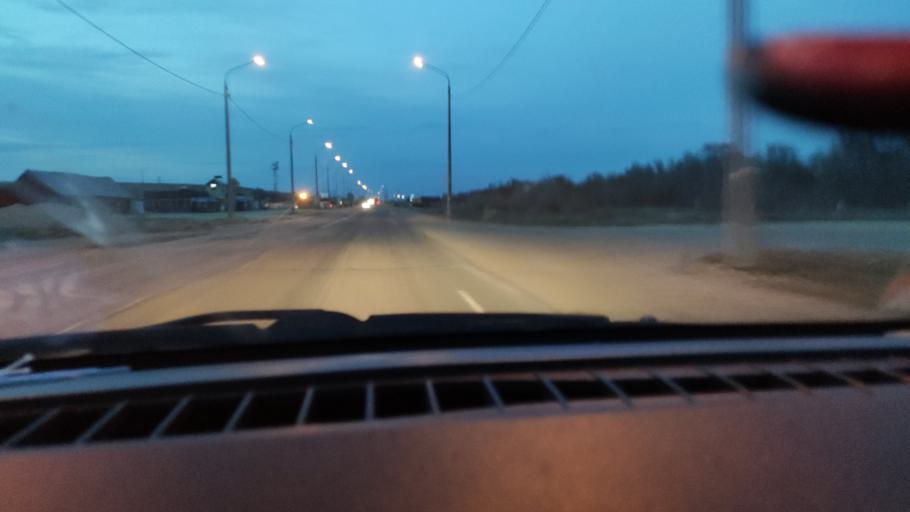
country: RU
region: Saratov
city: Sinodskoye
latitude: 52.0853
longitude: 46.8014
